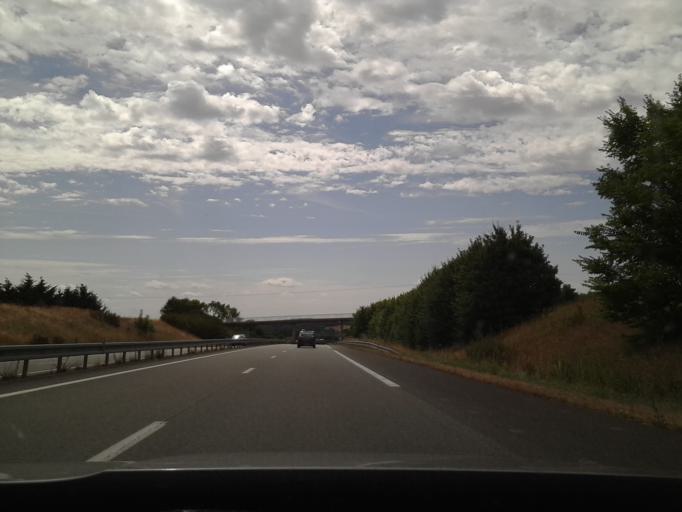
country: FR
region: Pays de la Loire
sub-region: Departement de la Sarthe
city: La Bazoge
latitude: 48.1115
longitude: 0.1562
